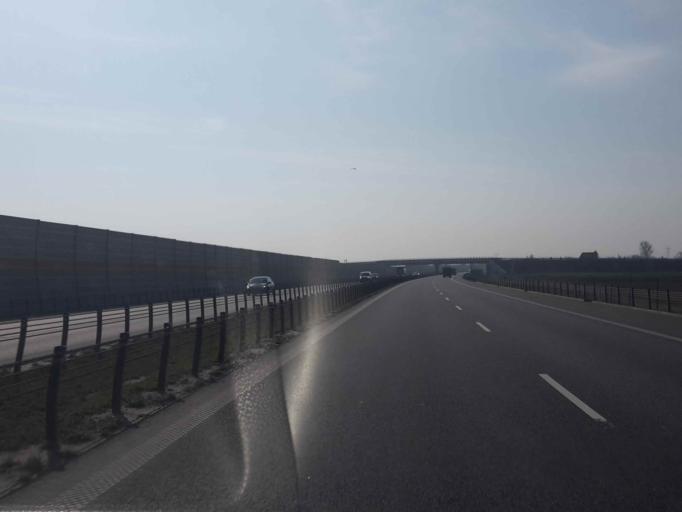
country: PL
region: Kujawsko-Pomorskie
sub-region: Powiat torunski
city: Lubicz Dolny
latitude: 53.0774
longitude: 18.7517
